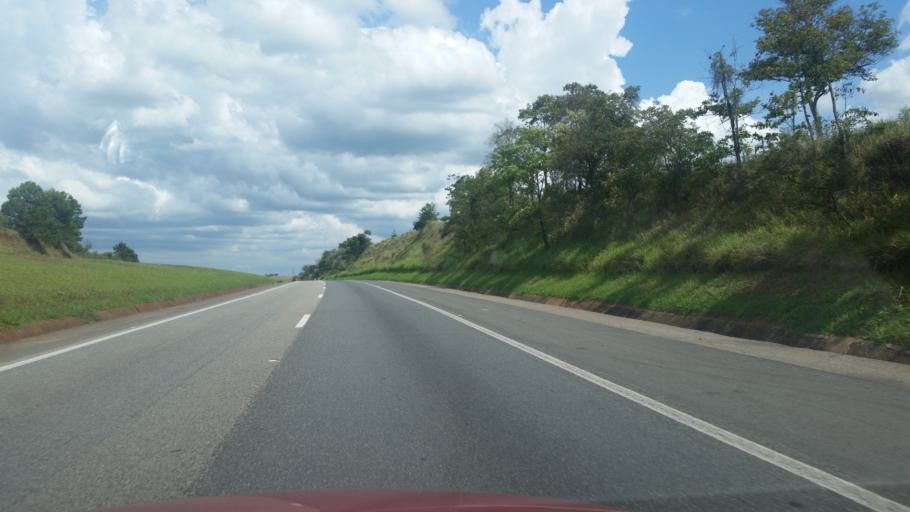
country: BR
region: Sao Paulo
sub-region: Tatui
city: Tatui
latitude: -23.2745
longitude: -47.8281
